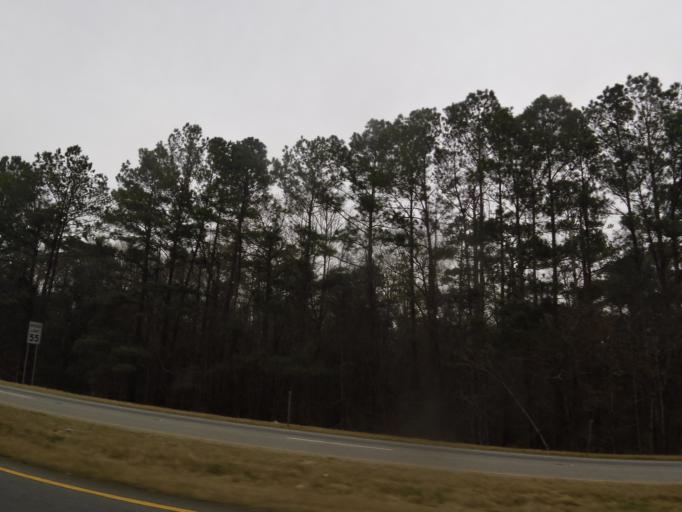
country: US
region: Georgia
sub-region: Thomas County
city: Thomasville
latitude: 30.8731
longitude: -84.0423
